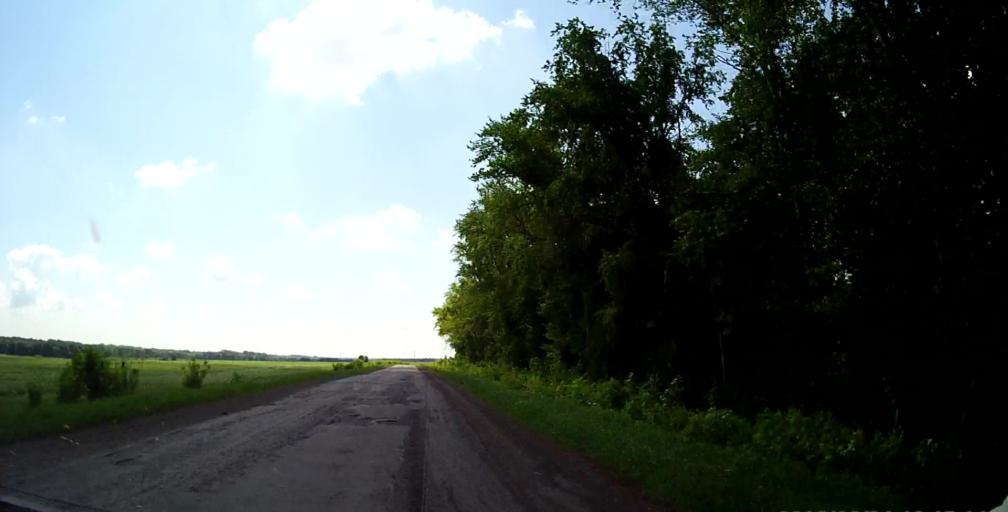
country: RU
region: Lipetsk
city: Chaplygin
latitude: 53.2991
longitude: 39.9532
